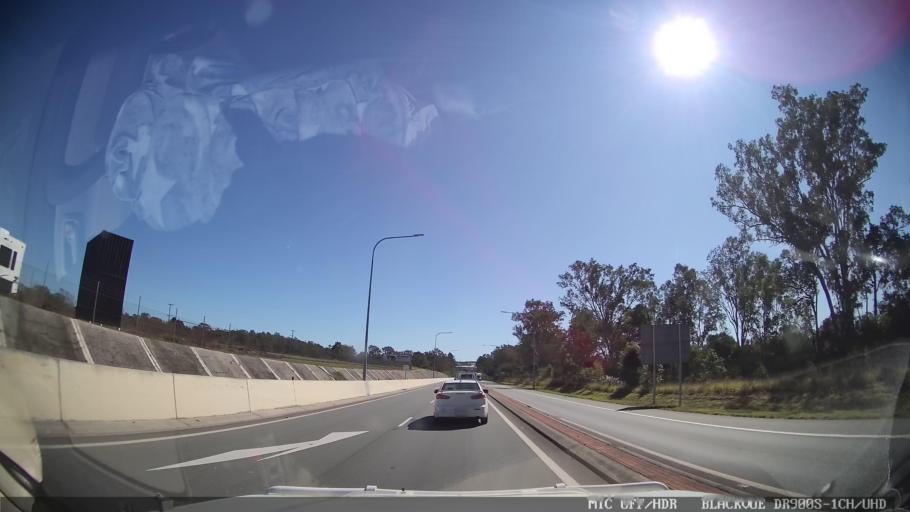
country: AU
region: Queensland
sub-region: Gympie Regional Council
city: Monkland
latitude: -26.2365
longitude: 152.6990
